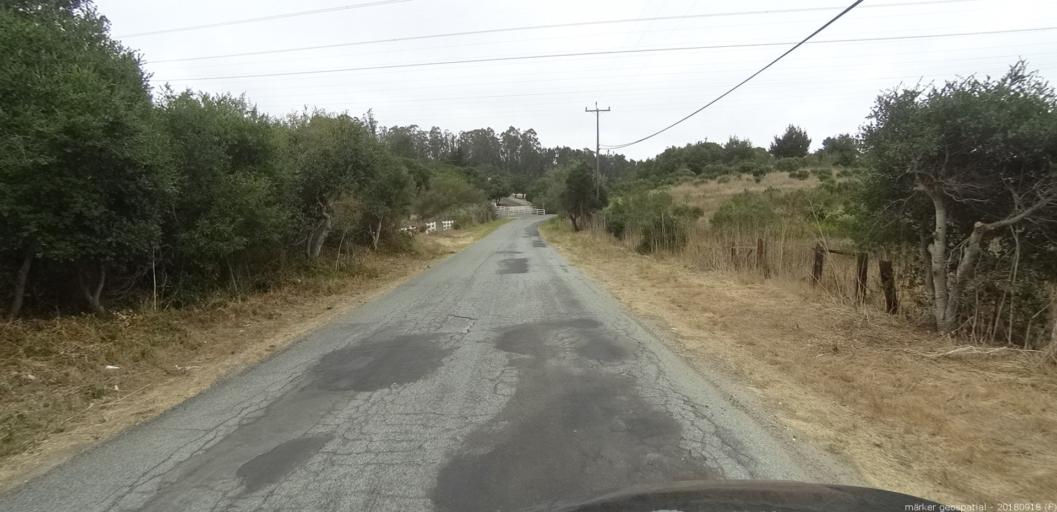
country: US
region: California
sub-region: Monterey County
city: Prunedale
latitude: 36.7803
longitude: -121.6494
